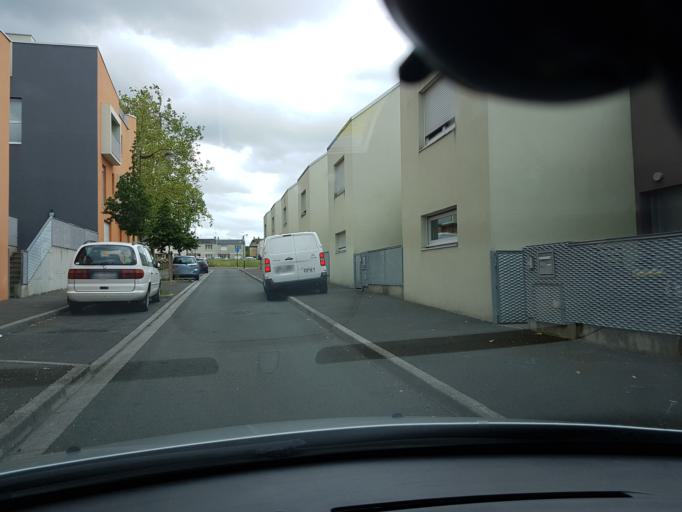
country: FR
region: Centre
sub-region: Departement du Cher
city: Bourges
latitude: 47.1093
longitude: 2.4105
